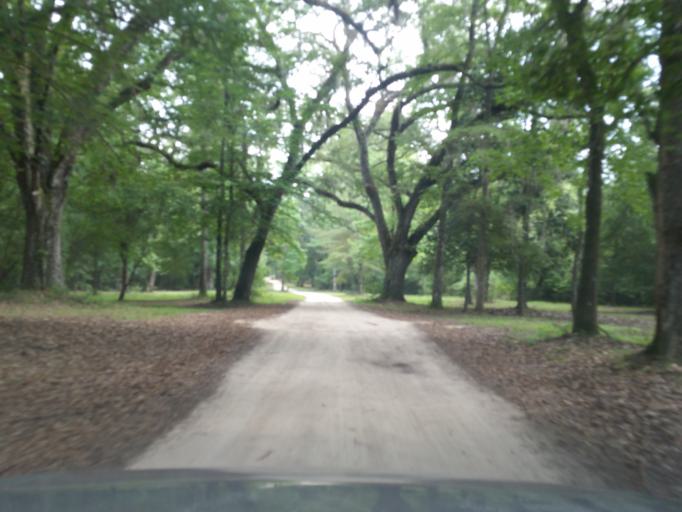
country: US
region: Alabama
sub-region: Baldwin County
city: Spanish Fort
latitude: 30.7464
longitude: -87.9234
